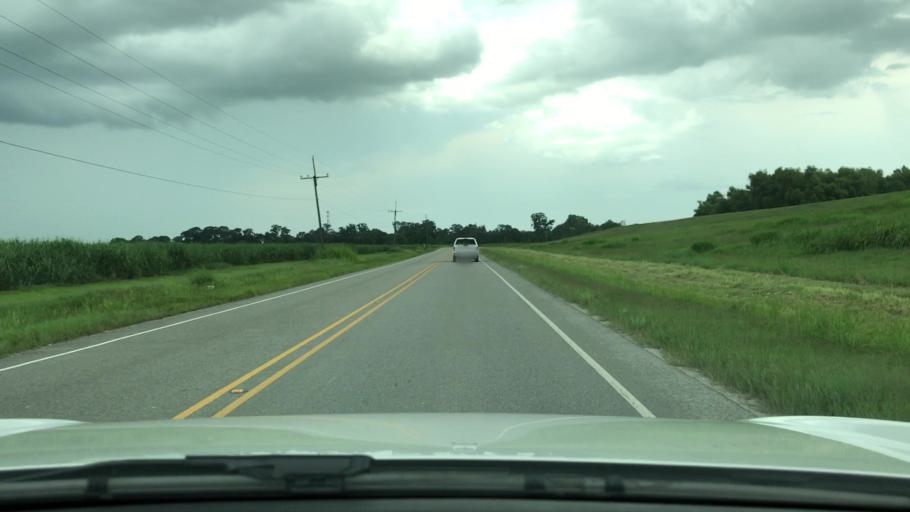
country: US
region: Louisiana
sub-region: Iberville Parish
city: Plaquemine
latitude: 30.2730
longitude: -91.2016
